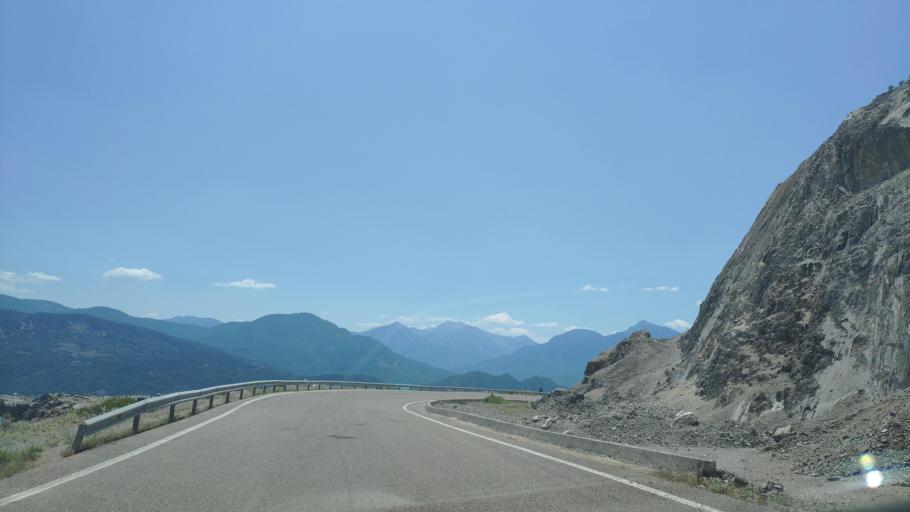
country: GR
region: Central Greece
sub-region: Nomos Evrytanias
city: Kerasochori
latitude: 38.9559
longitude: 21.4663
